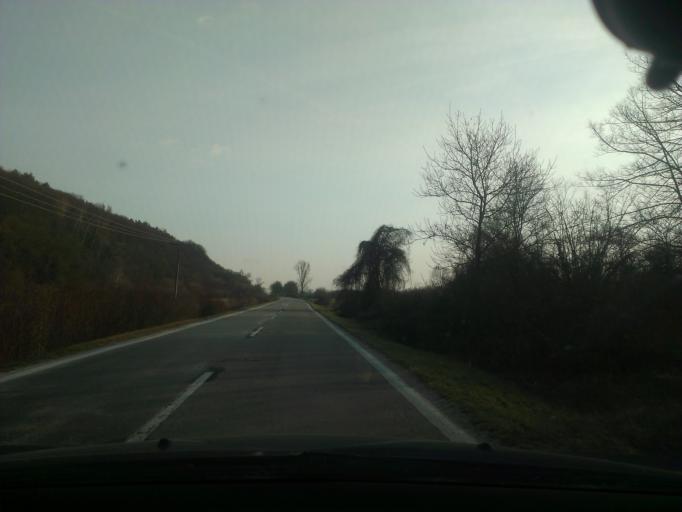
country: SK
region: Trenciansky
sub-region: Okres Nove Mesto nad Vahom
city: Nove Mesto nad Vahom
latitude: 48.6854
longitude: 17.8780
